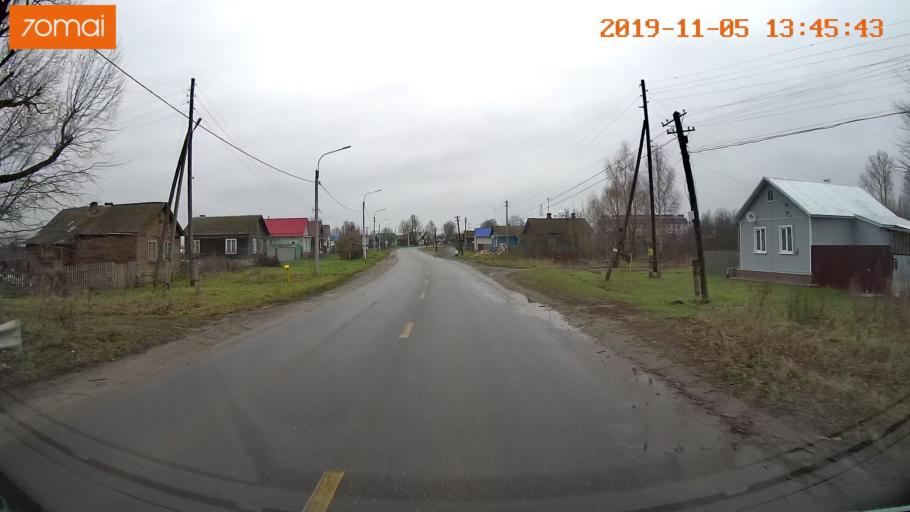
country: RU
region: Ivanovo
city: Shuya
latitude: 56.9909
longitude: 41.4118
